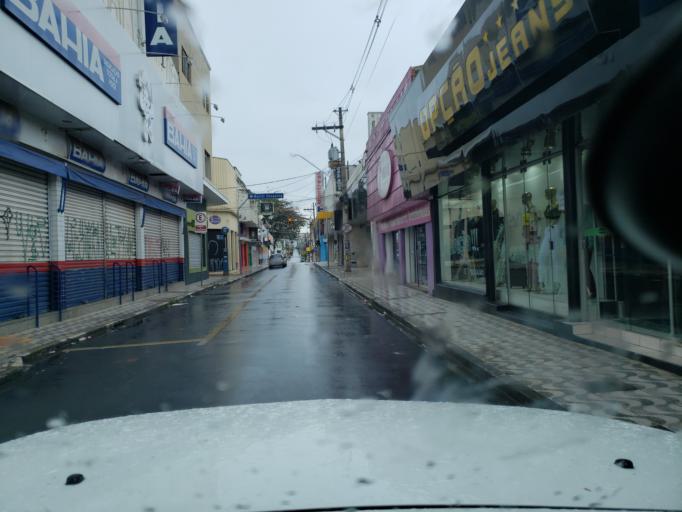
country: BR
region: Sao Paulo
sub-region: Moji-Guacu
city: Mogi-Gaucu
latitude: -22.3721
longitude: -46.9417
